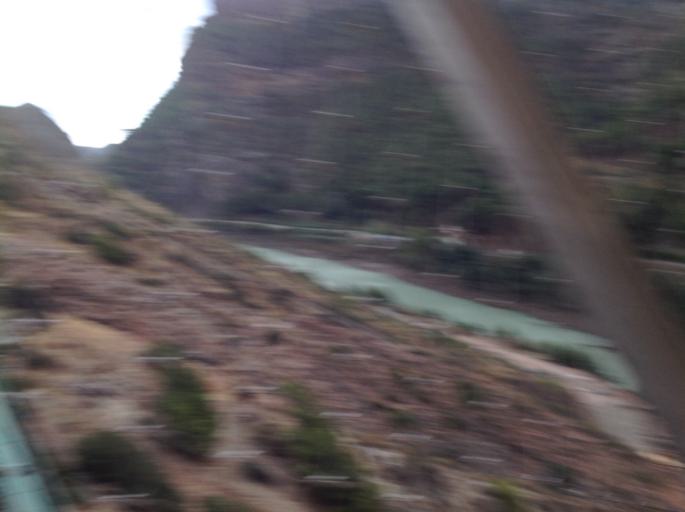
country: ES
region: Andalusia
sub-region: Provincia de Malaga
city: Carratraca
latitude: 36.9161
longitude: -4.7710
